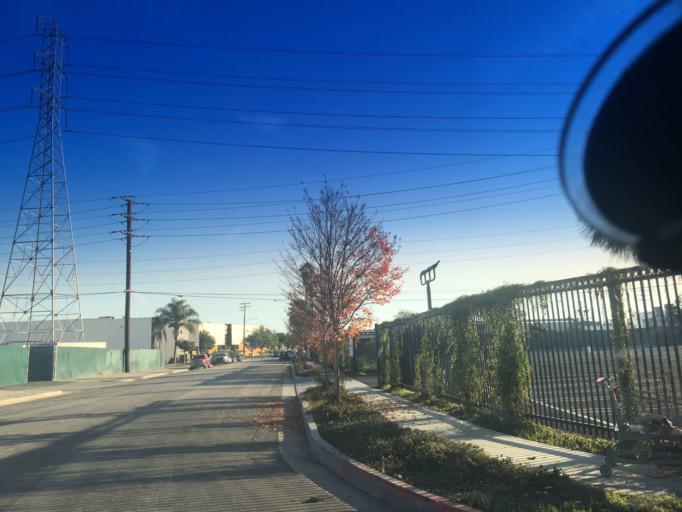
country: US
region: California
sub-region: Orange County
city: Anaheim
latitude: 33.8080
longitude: -117.9025
